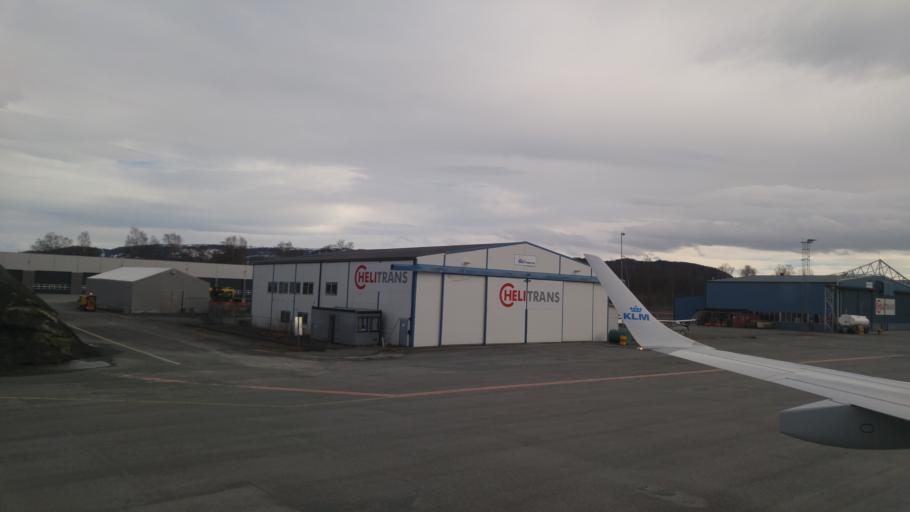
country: NO
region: Nord-Trondelag
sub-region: Stjordal
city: Stjordalshalsen
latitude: 63.4549
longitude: 10.9239
